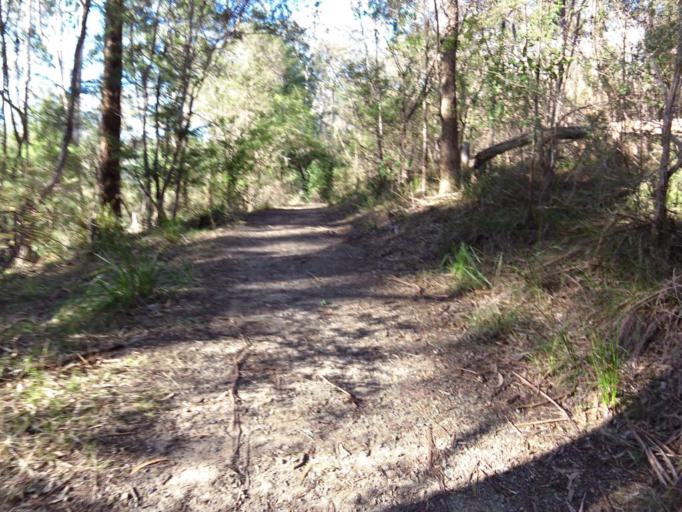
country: AU
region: Victoria
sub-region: Nillumbik
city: North Warrandyte
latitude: -37.7310
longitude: 145.2013
